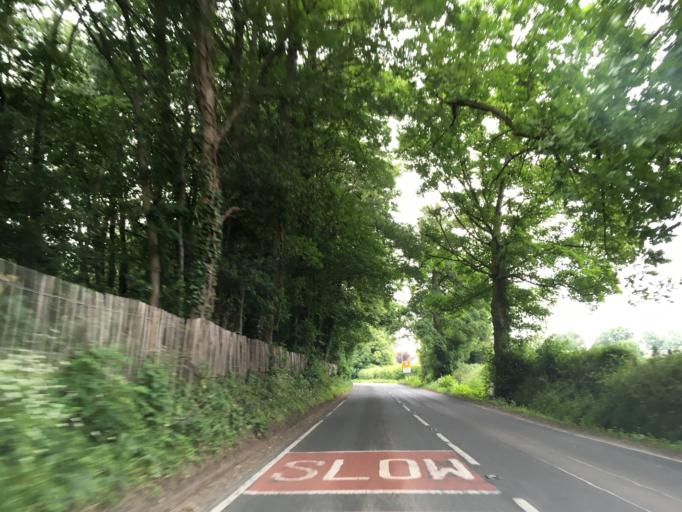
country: GB
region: England
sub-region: Gloucestershire
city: Stonehouse
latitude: 51.7701
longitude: -2.3595
